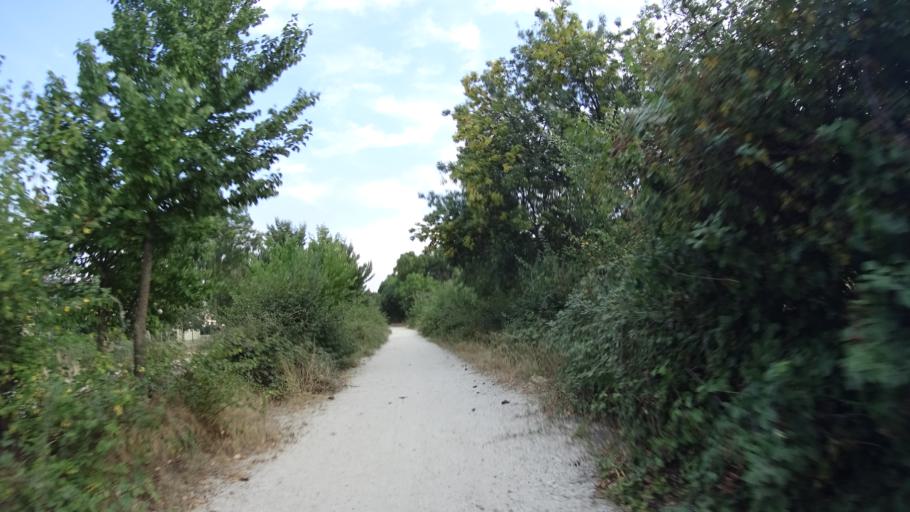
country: ES
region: Madrid
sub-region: Provincia de Madrid
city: Moralzarzal
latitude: 40.6877
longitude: -3.9739
